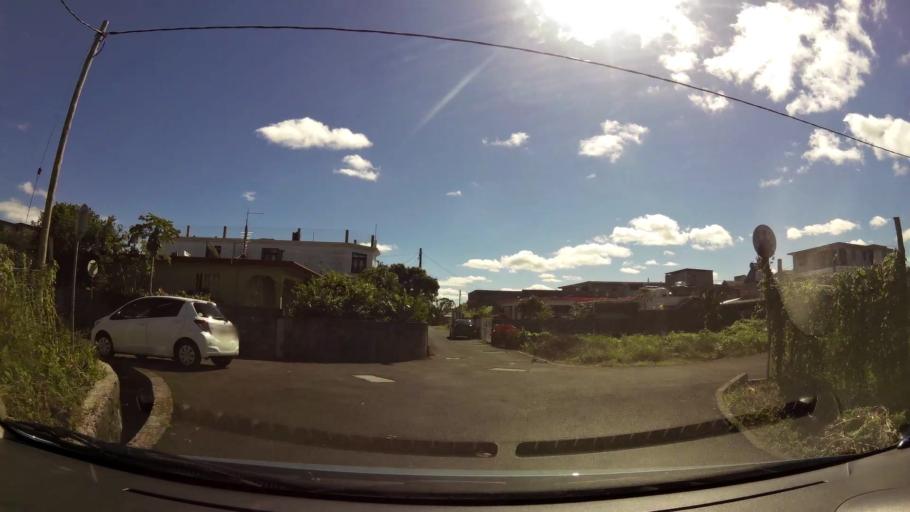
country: MU
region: Plaines Wilhems
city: Vacoas
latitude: -20.3351
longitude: 57.4779
